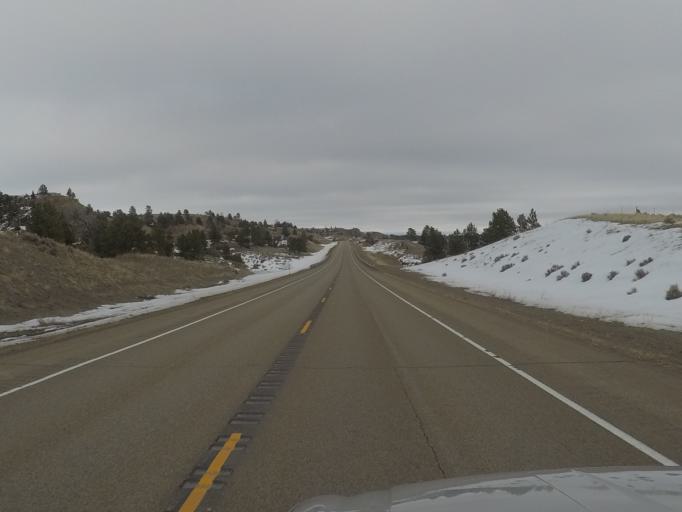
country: US
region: Montana
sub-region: Golden Valley County
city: Ryegate
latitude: 46.3168
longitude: -109.1458
